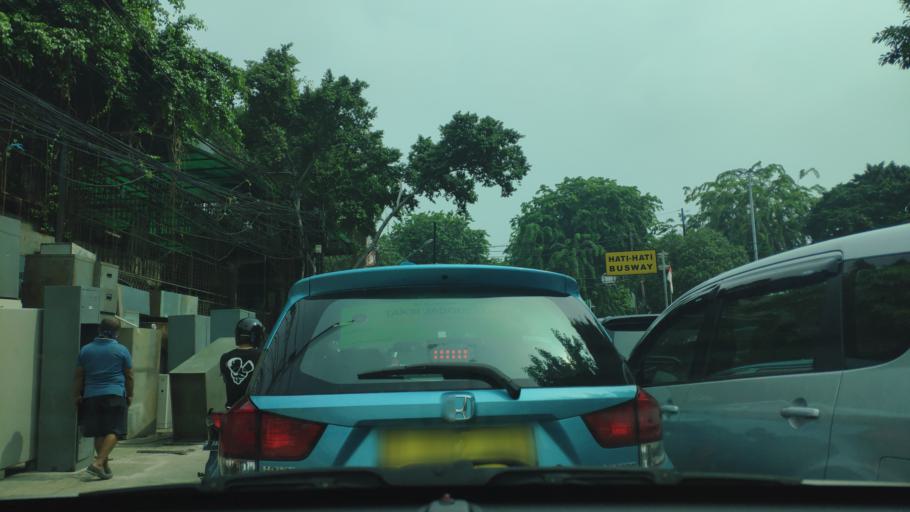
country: ID
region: Jakarta Raya
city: Jakarta
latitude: -6.1649
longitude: 106.8132
